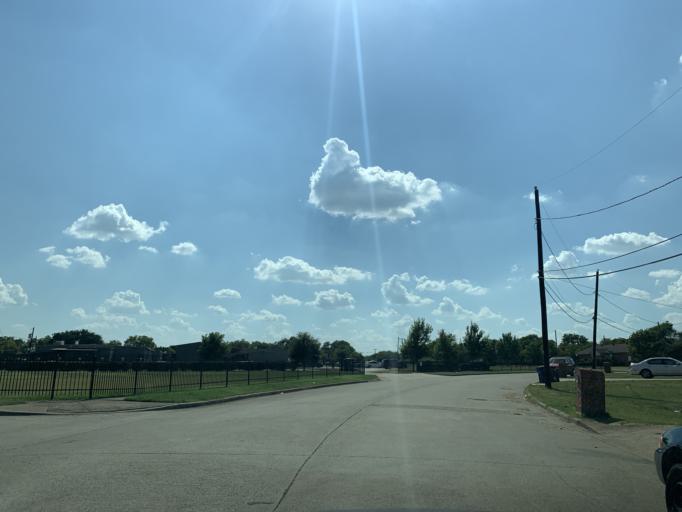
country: US
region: Texas
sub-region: Dallas County
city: Hutchins
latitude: 32.6546
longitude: -96.7733
